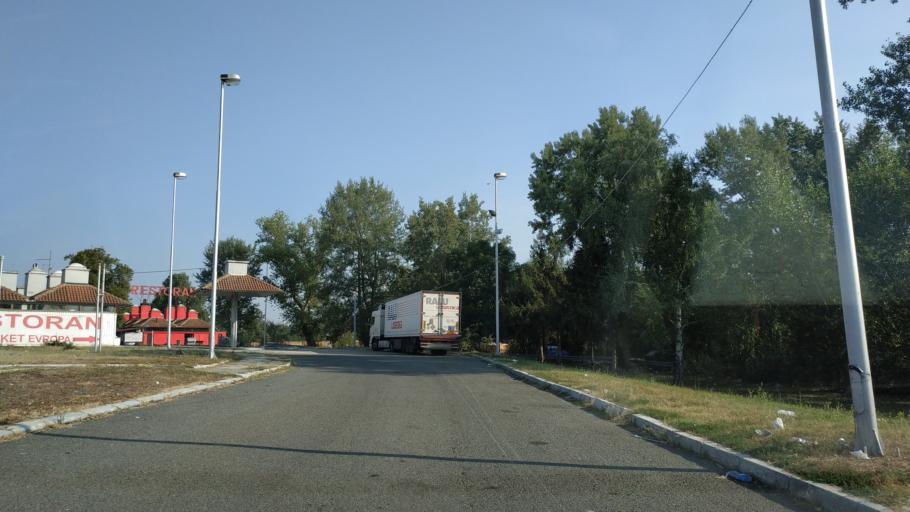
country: RS
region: Central Serbia
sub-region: Podunavski Okrug
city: Velika Plana
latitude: 44.3485
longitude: 21.0771
